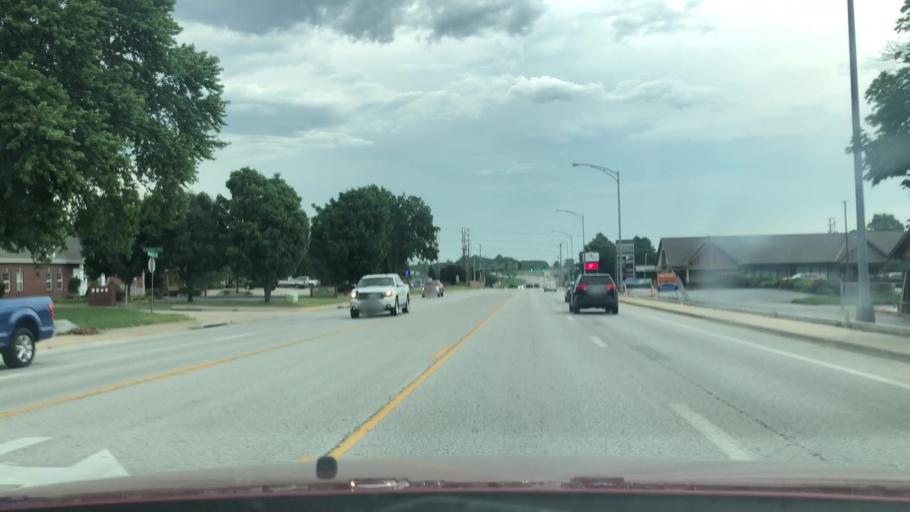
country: US
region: Missouri
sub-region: Greene County
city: Springfield
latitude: 37.1374
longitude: -93.2656
